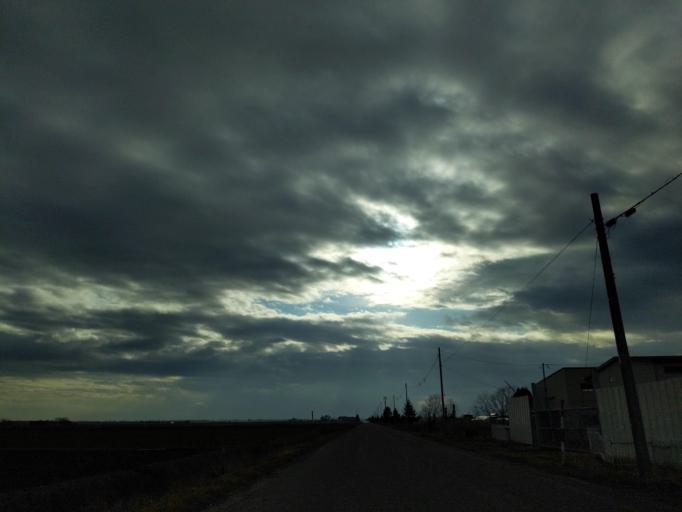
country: JP
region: Hokkaido
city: Kitahiroshima
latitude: 43.0018
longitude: 141.6638
